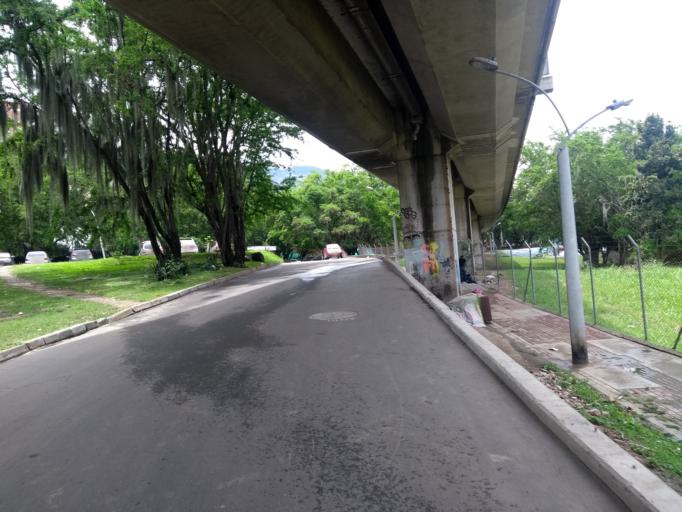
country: CO
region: Antioquia
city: Bello
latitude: 6.3338
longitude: -75.5500
